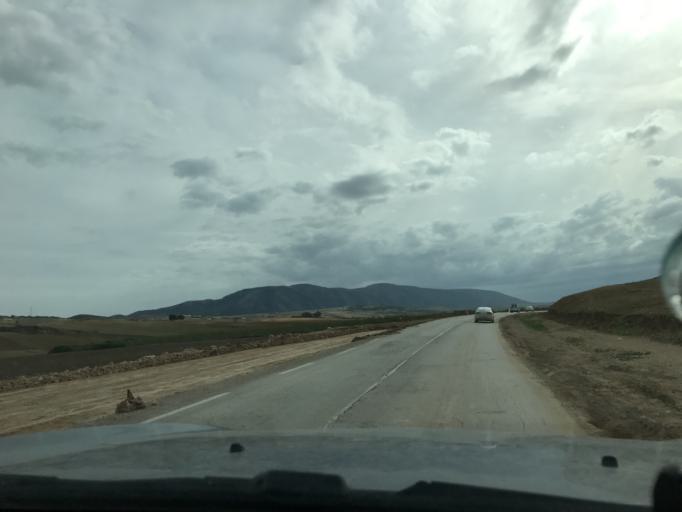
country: TN
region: Silyanah
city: Bu `Aradah
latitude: 36.1554
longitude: 9.6376
